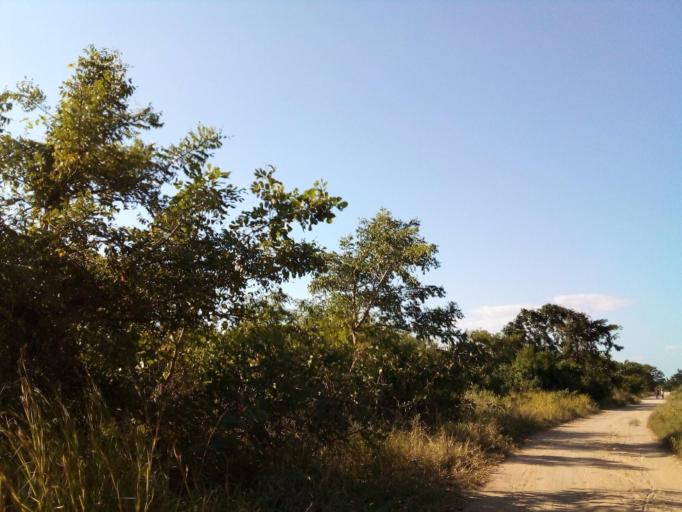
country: MZ
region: Zambezia
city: Quelimane
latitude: -17.5243
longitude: 36.6817
